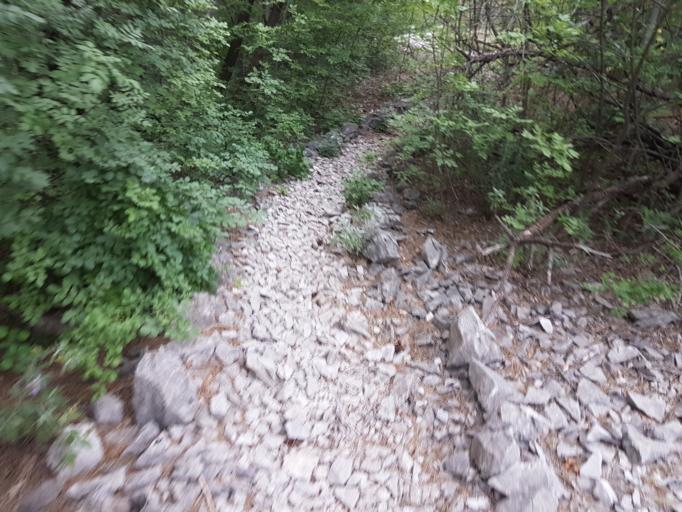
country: IT
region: Friuli Venezia Giulia
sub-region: Provincia di Trieste
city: Aurisina
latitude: 45.7461
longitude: 13.6676
